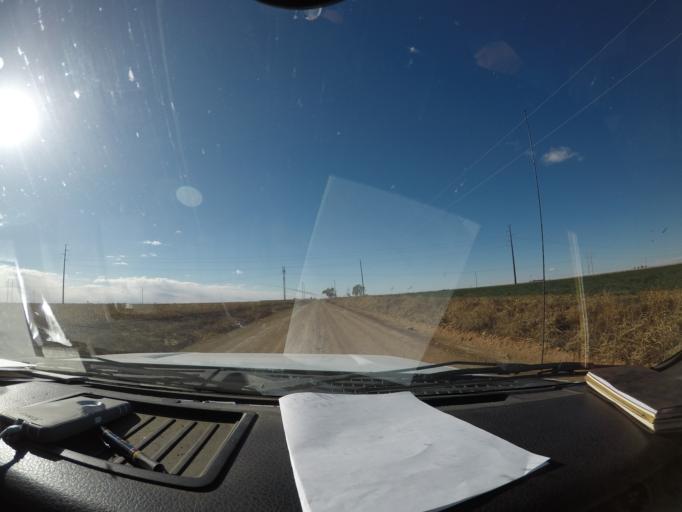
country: US
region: New Mexico
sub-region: Curry County
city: Clovis
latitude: 34.5797
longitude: -103.1421
